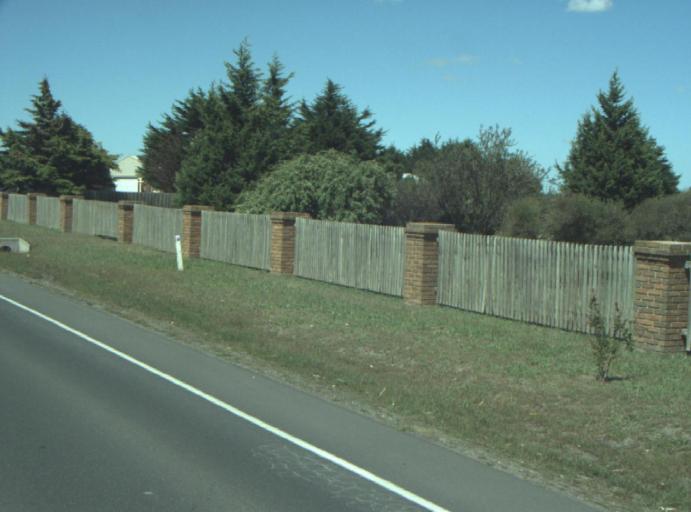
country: AU
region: Victoria
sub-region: Greater Geelong
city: Breakwater
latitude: -38.1882
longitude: 144.3541
